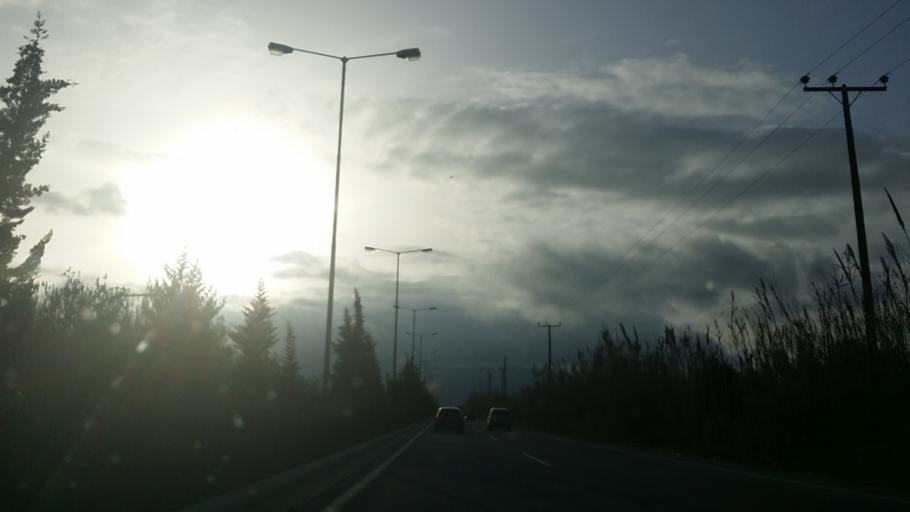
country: GR
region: Attica
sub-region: Nomarchia Anatolikis Attikis
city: Keratea
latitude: 37.8032
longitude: 24.0341
